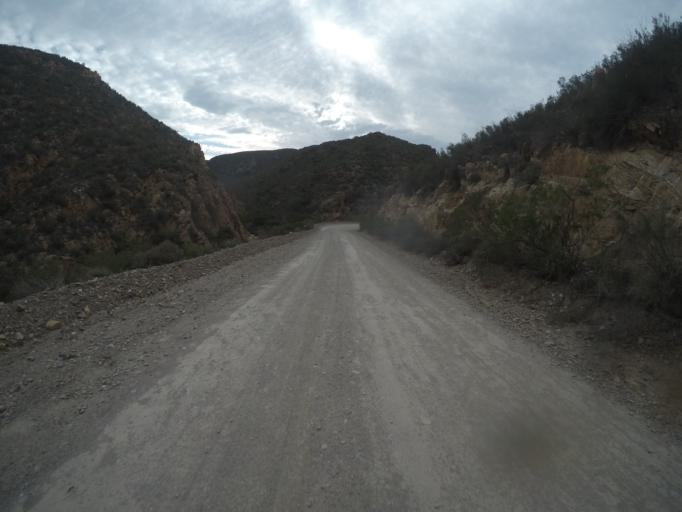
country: ZA
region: Eastern Cape
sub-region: Cacadu District Municipality
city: Willowmore
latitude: -33.5066
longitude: 23.6356
